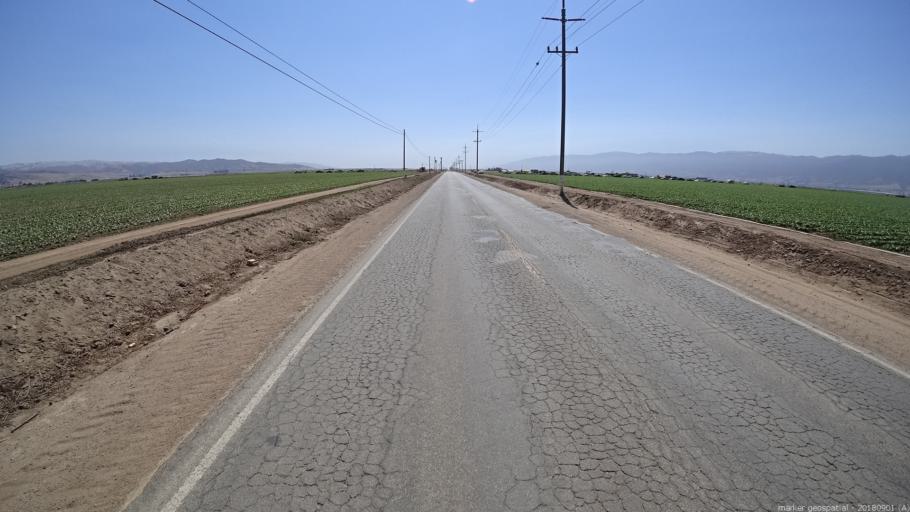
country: US
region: California
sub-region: Monterey County
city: Chualar
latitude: 36.6156
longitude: -121.5219
